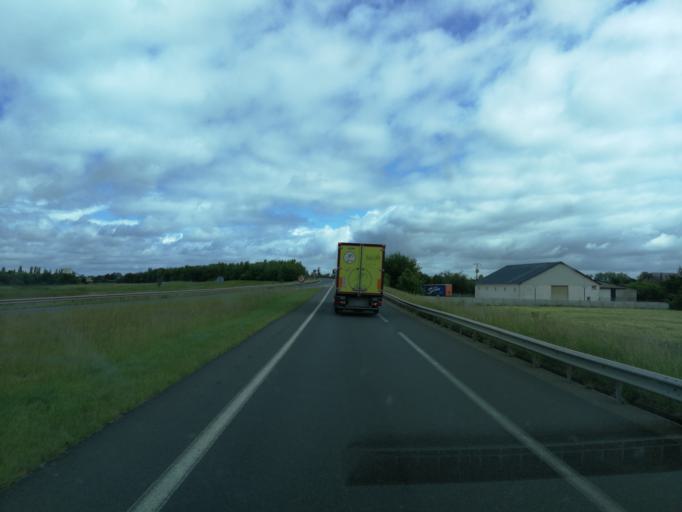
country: FR
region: Haute-Normandie
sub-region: Departement de l'Eure
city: Evreux
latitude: 49.0075
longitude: 1.1916
